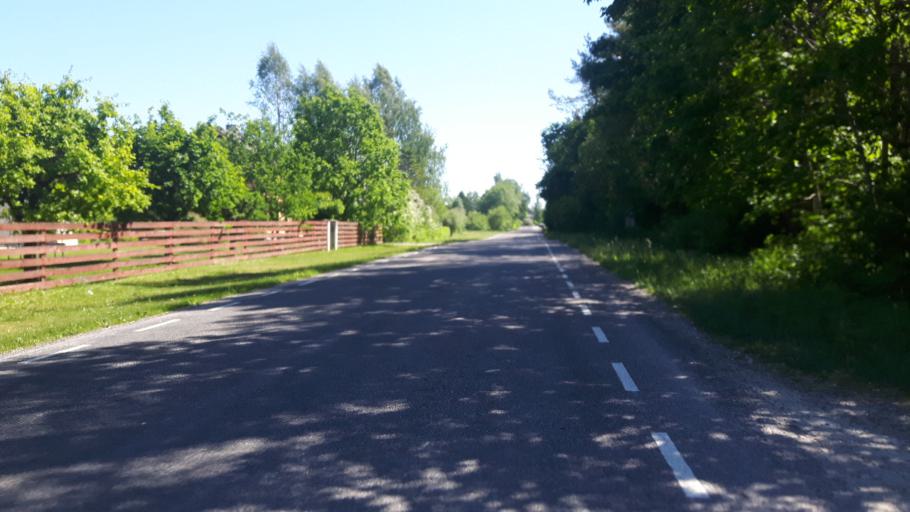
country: EE
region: Raplamaa
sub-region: Kohila vald
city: Kohila
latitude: 59.1732
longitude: 24.7346
